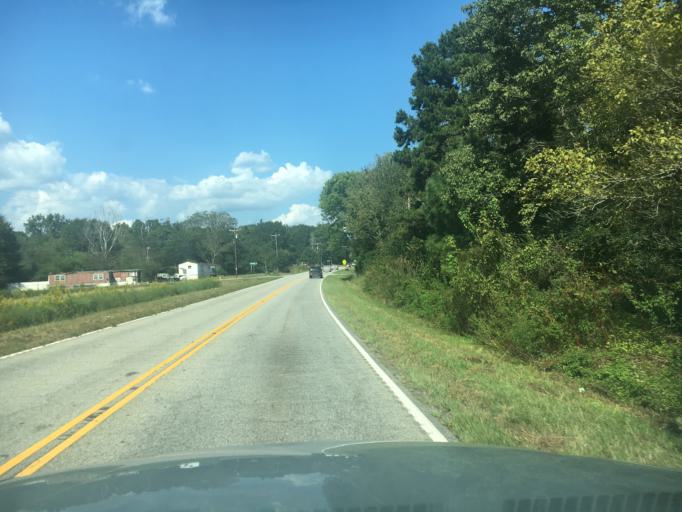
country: US
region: South Carolina
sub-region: Anderson County
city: Pendleton
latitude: 34.6096
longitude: -82.7891
